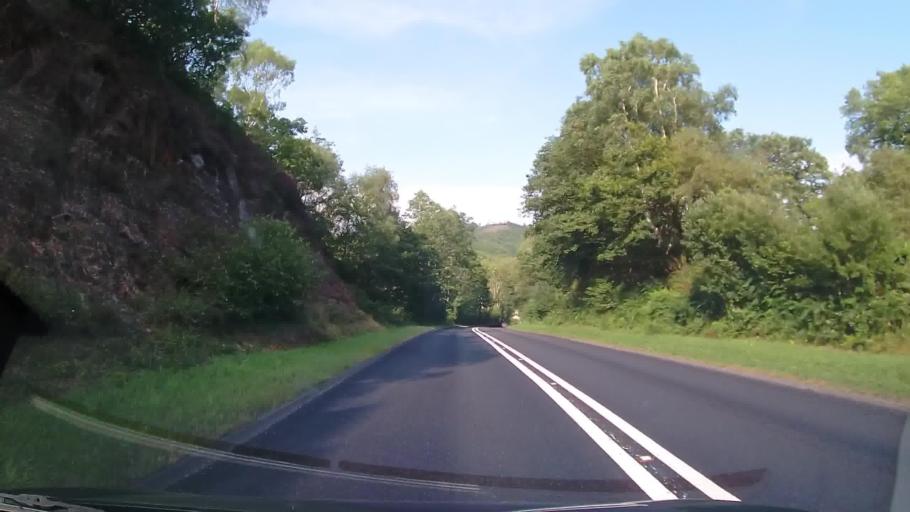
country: GB
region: Wales
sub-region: Gwynedd
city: Penrhyndeudraeth
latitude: 52.9405
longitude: -4.0452
